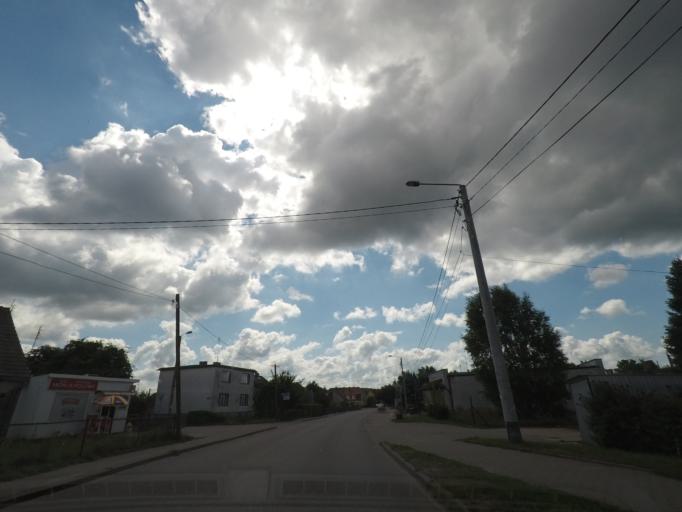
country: PL
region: Pomeranian Voivodeship
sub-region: Powiat wejherowski
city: Leczyce
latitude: 54.5846
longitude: 17.8637
